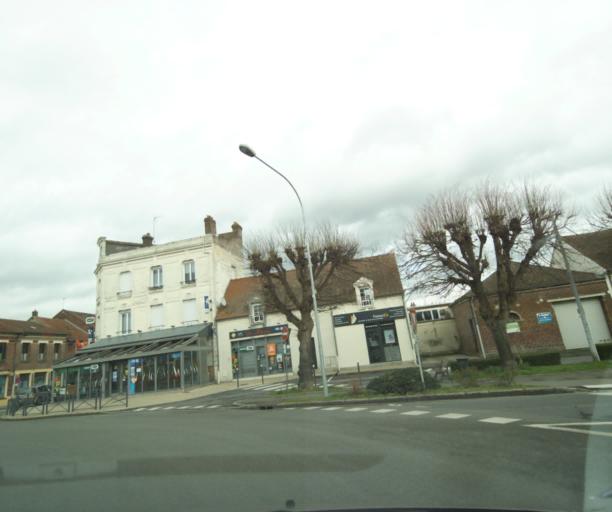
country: FR
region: Picardie
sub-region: Departement de l'Oise
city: Noyon
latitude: 49.5783
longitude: 2.9947
